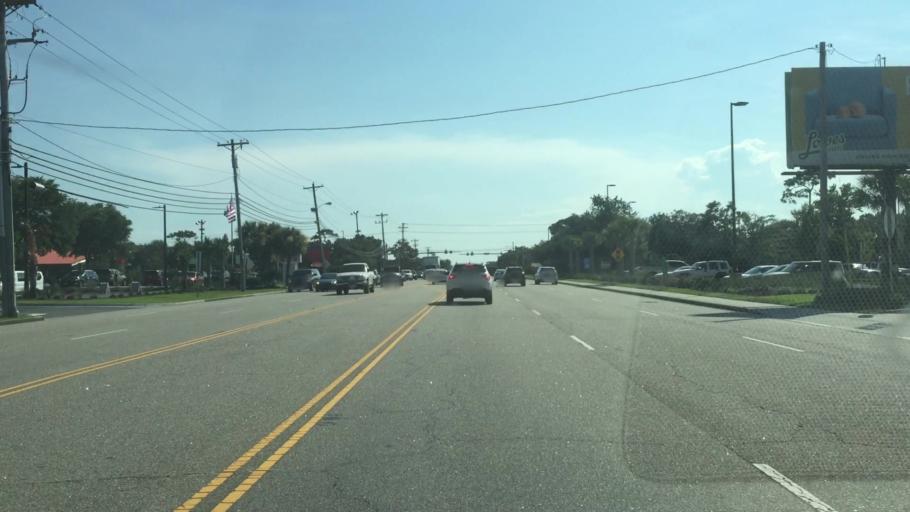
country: US
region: South Carolina
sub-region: Horry County
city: Myrtle Beach
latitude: 33.7507
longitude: -78.8144
